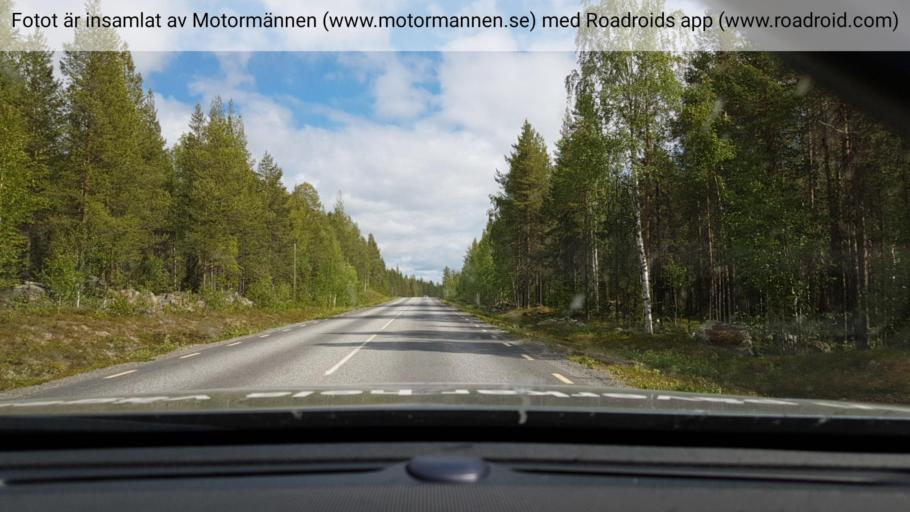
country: SE
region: Vaesterbotten
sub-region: Sorsele Kommun
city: Sorsele
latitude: 65.6916
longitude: 17.1872
